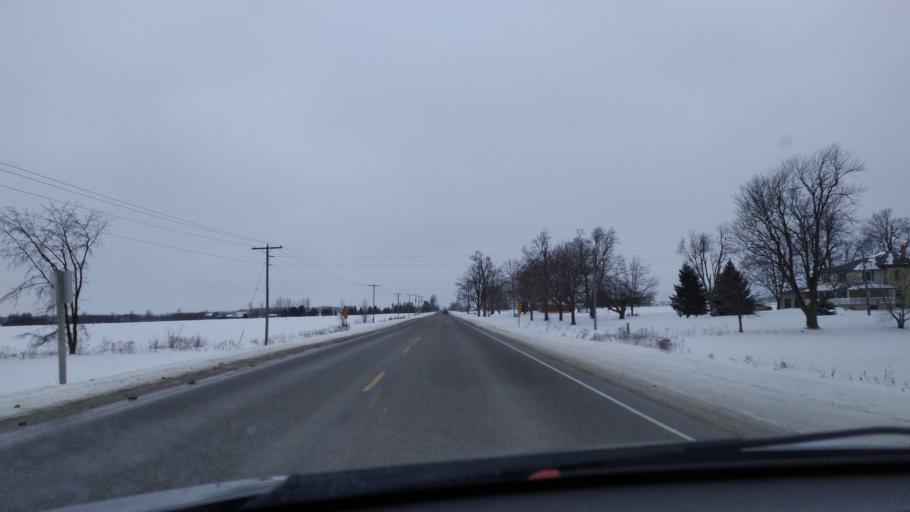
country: CA
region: Ontario
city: North Perth
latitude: 43.5921
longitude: -80.8837
